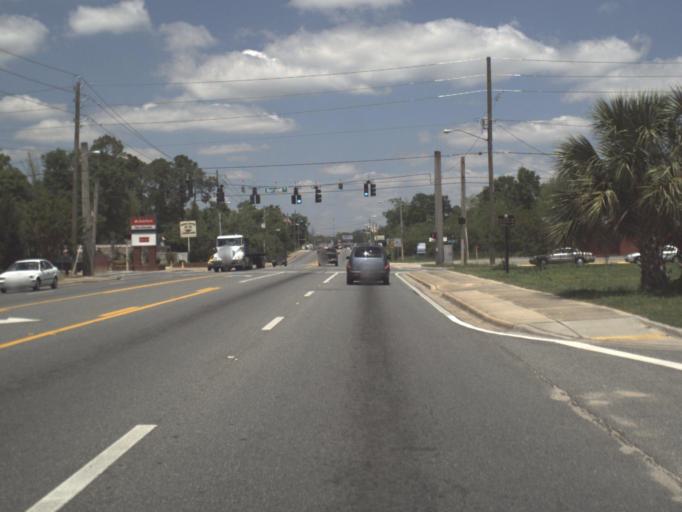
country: US
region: Florida
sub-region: Santa Rosa County
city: Milton
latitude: 30.6247
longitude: -87.0430
